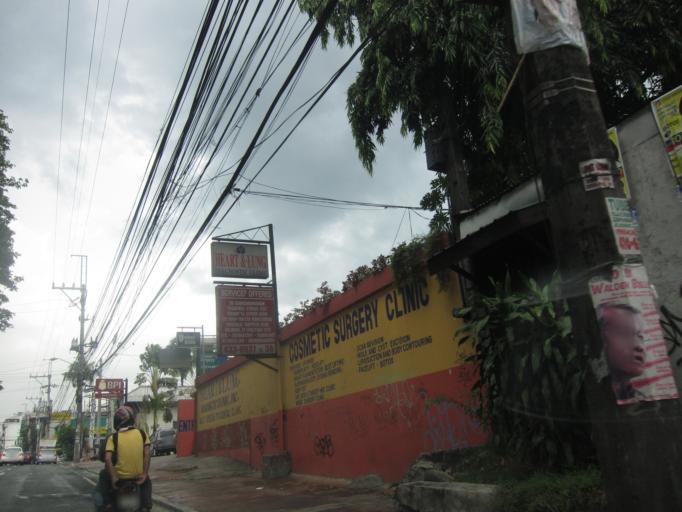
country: PH
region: Metro Manila
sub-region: Quezon City
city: Quezon City
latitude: 14.6446
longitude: 121.0537
